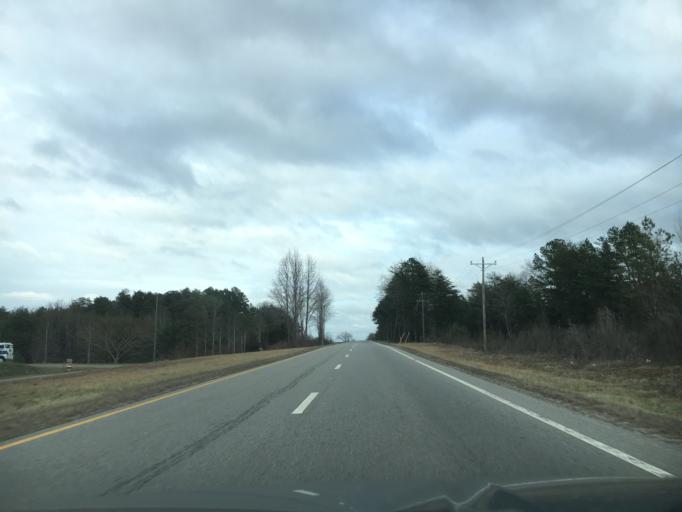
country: US
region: Virginia
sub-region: Prince Edward County
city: Hampden Sydney
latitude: 37.0879
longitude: -78.4002
